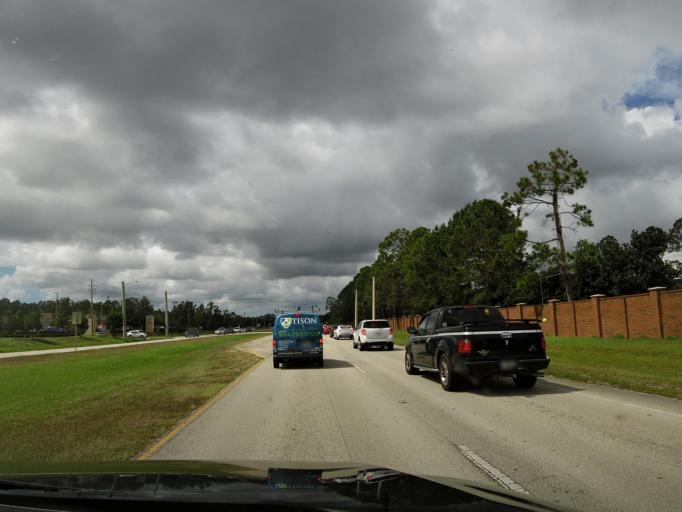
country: US
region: Florida
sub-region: Clay County
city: Lakeside
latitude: 30.1024
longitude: -81.7186
